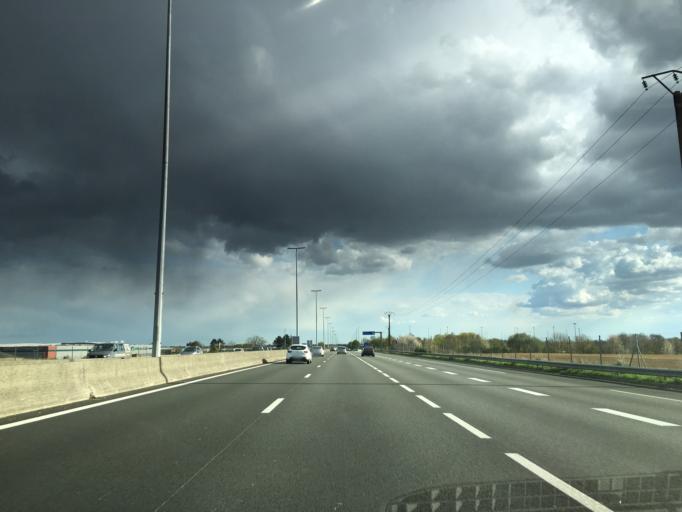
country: FR
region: Ile-de-France
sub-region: Departement du Val-d'Oise
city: Vemars
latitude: 49.0787
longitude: 2.5515
